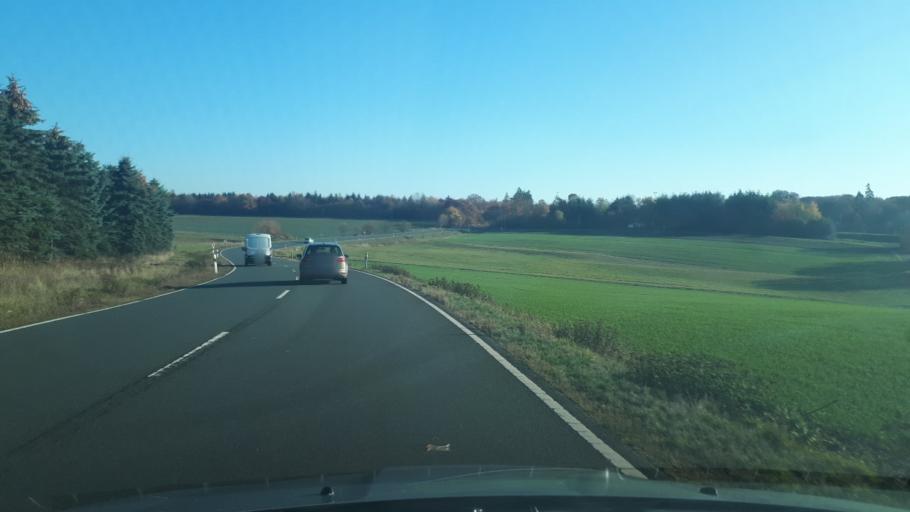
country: DE
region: Rheinland-Pfalz
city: Buchel
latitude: 50.1687
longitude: 7.0922
